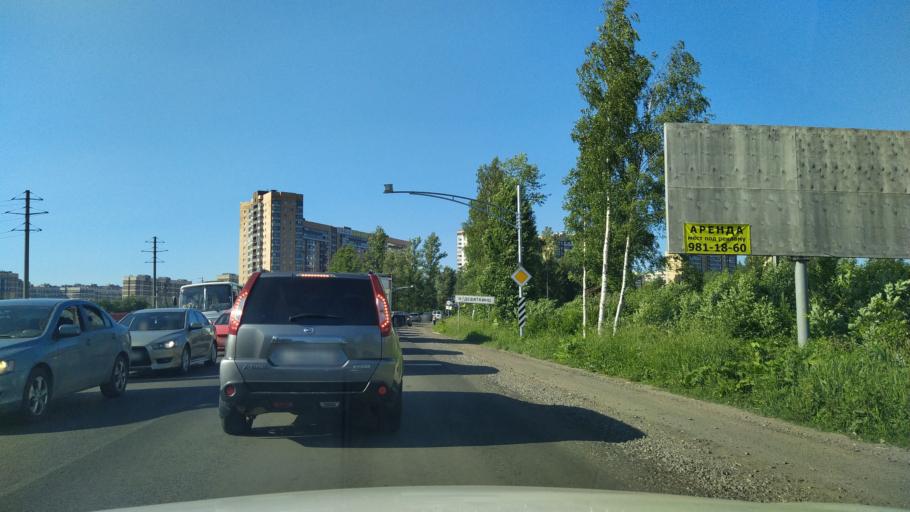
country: RU
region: Leningrad
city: Murino
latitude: 60.0528
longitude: 30.4657
